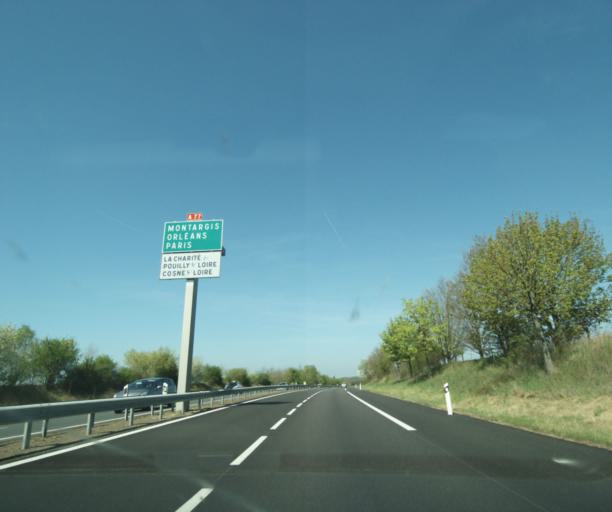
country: FR
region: Bourgogne
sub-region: Departement de la Nievre
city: Chaulgnes
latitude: 47.1305
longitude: 3.0457
